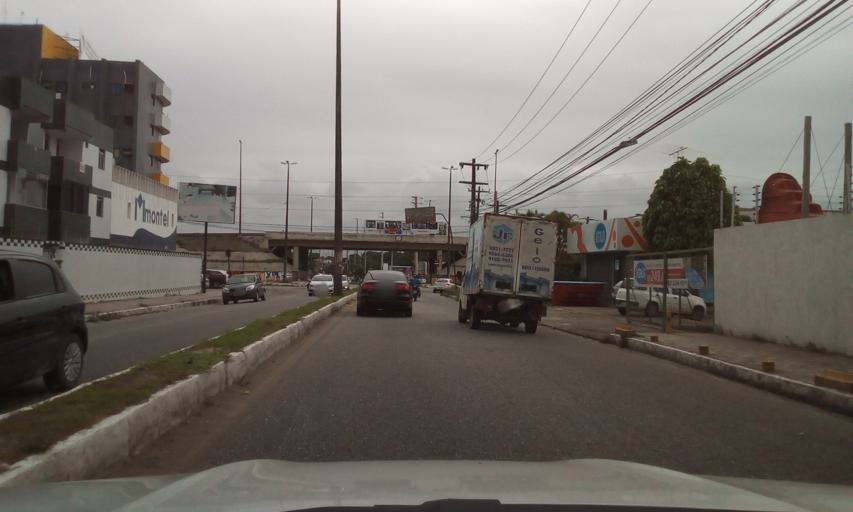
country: BR
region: Paraiba
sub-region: Joao Pessoa
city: Joao Pessoa
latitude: -7.0981
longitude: -34.8468
